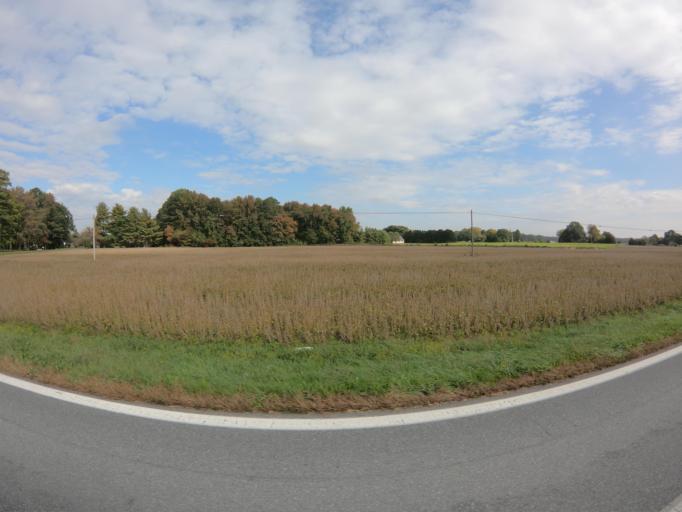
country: US
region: Maryland
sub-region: Caroline County
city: Denton
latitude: 38.8395
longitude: -75.7879
